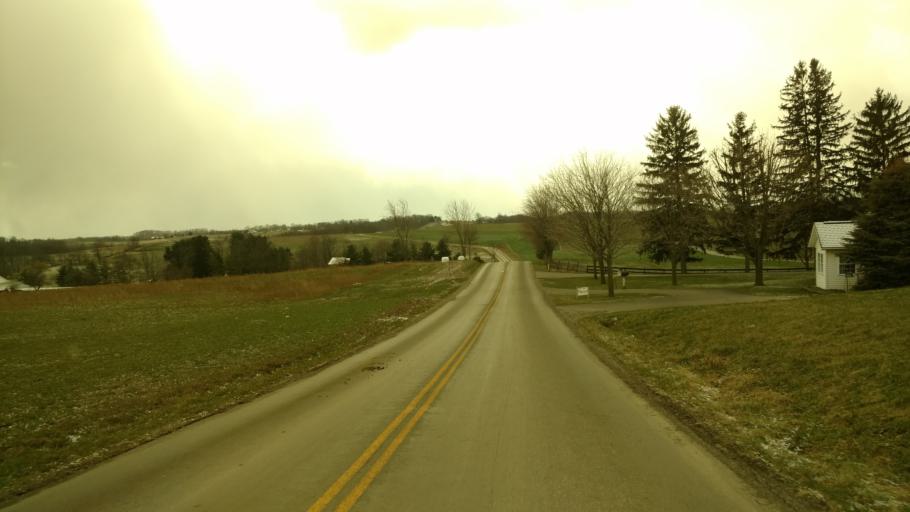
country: US
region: Ohio
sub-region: Tuscarawas County
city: Sugarcreek
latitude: 40.4694
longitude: -81.7787
